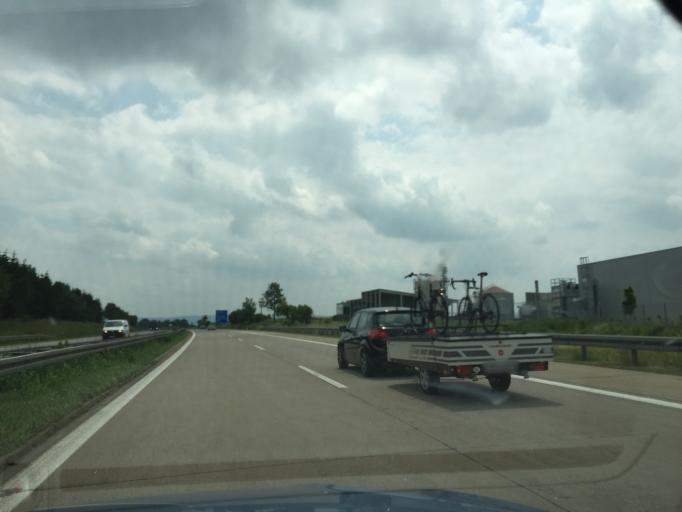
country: DE
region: Baden-Wuerttemberg
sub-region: Regierungsbezirk Stuttgart
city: Ellwangen
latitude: 48.9625
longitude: 10.1847
